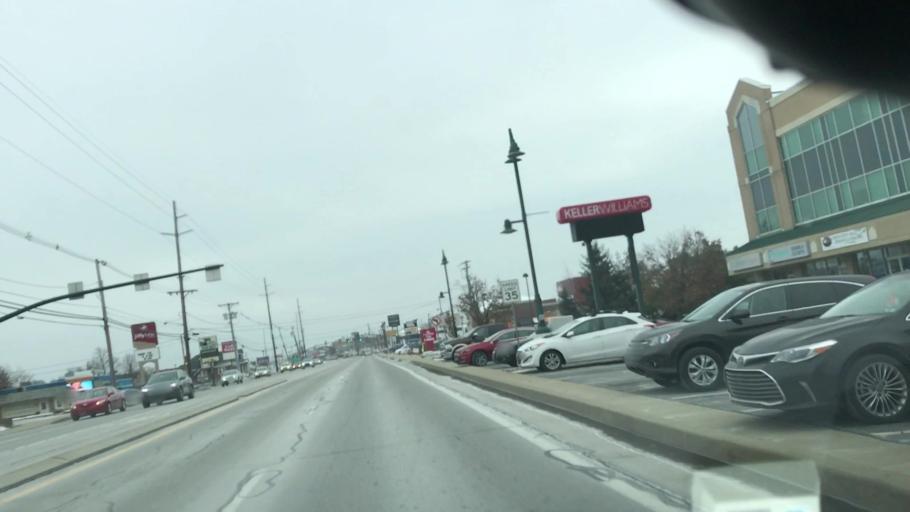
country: US
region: Pennsylvania
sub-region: Allegheny County
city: Bradford Woods
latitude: 40.6215
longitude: -80.0545
